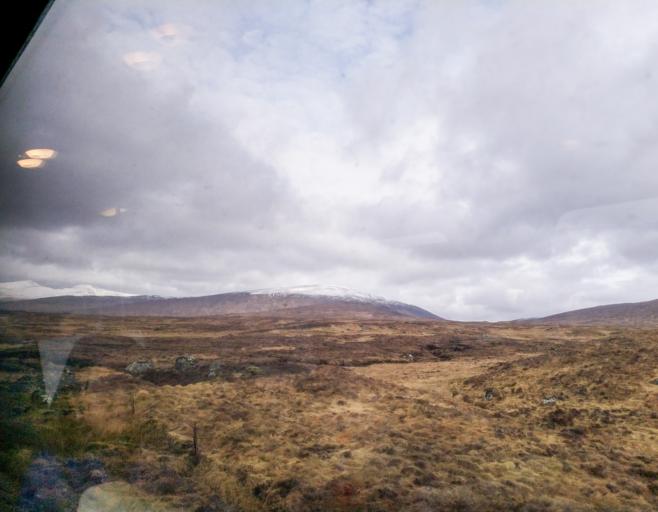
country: GB
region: Scotland
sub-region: Highland
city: Spean Bridge
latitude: 56.7283
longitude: -4.6425
